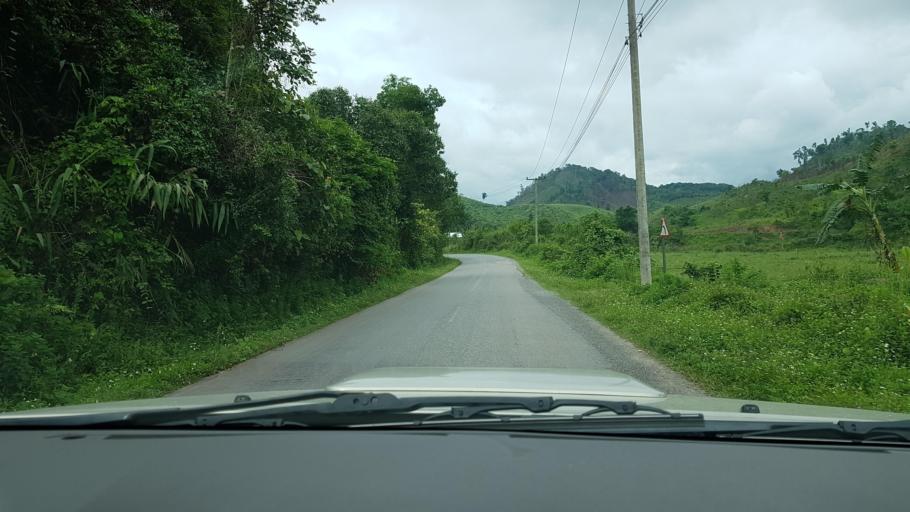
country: LA
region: Oudomxai
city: Muang Xay
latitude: 20.5476
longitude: 101.9075
